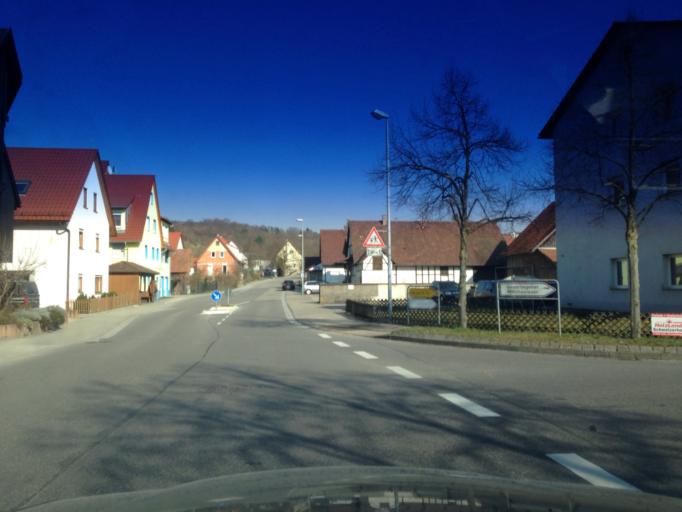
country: DE
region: Baden-Wuerttemberg
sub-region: Regierungsbezirk Stuttgart
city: Eberdingen
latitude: 48.8809
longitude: 8.9641
